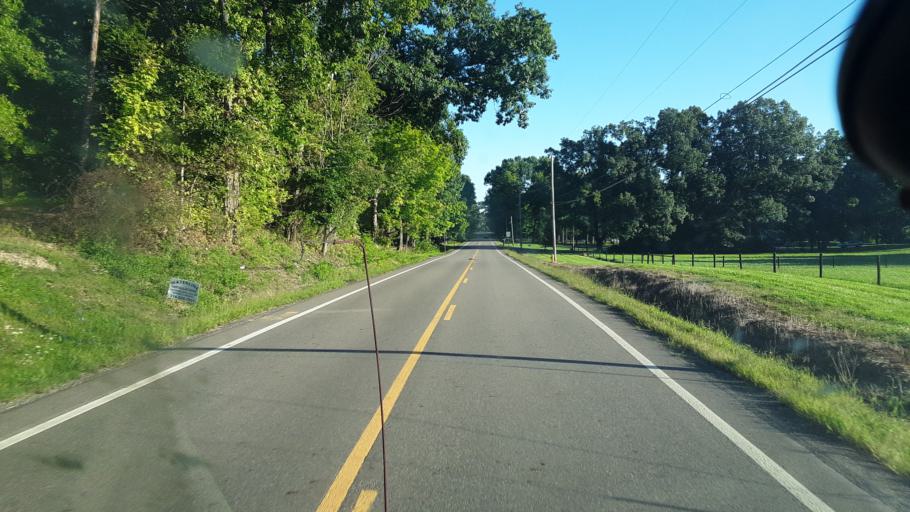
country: US
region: Ohio
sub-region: Trumbull County
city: Leavittsburg
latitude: 41.3113
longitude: -80.9558
